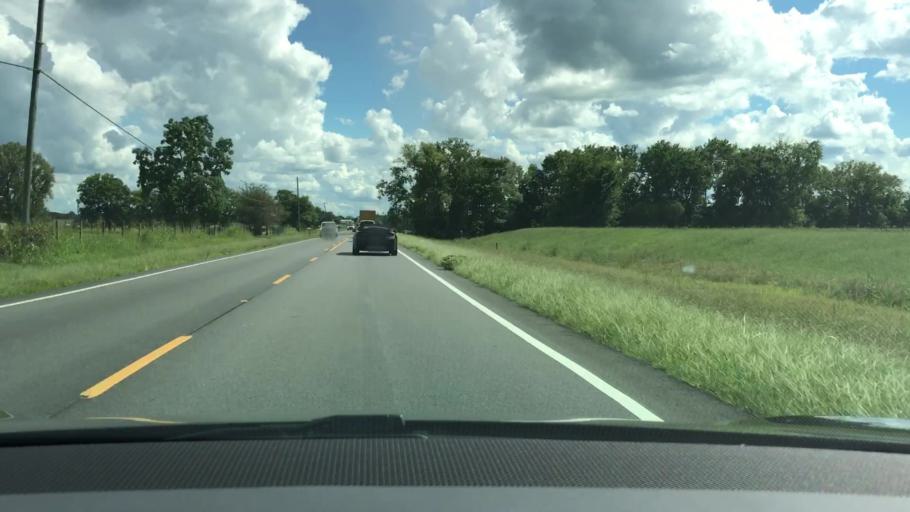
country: US
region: Alabama
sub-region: Montgomery County
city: Pike Road
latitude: 32.3001
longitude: -86.1027
